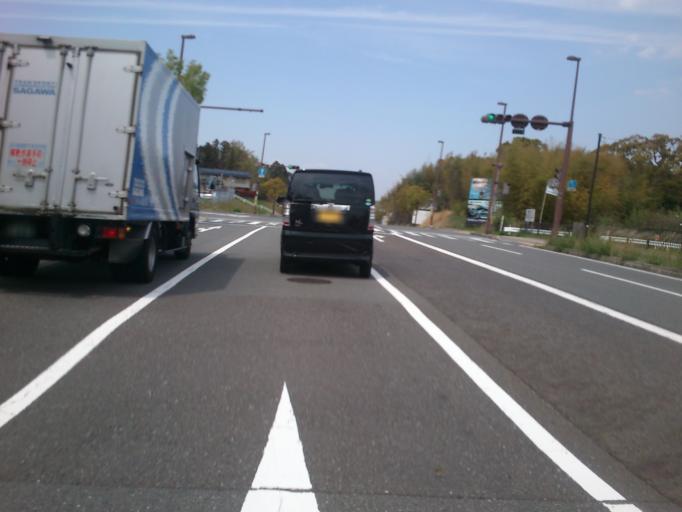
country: JP
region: Nara
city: Nara-shi
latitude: 34.7525
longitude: 135.7879
